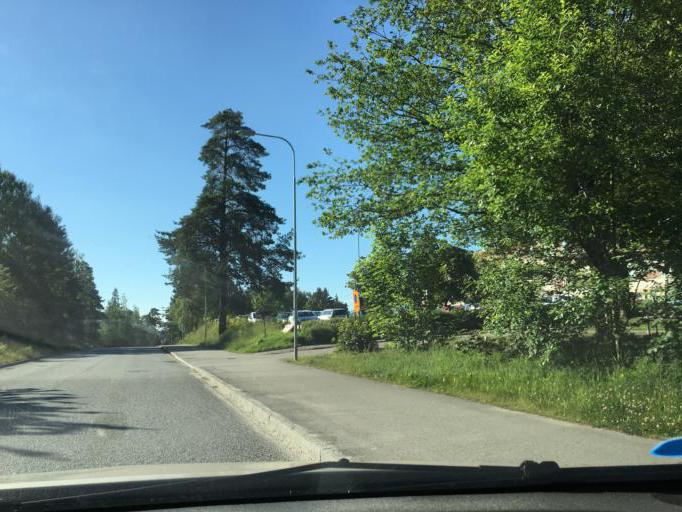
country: SE
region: Stockholm
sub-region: Sodertalje Kommun
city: Pershagen
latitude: 59.1888
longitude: 17.6654
